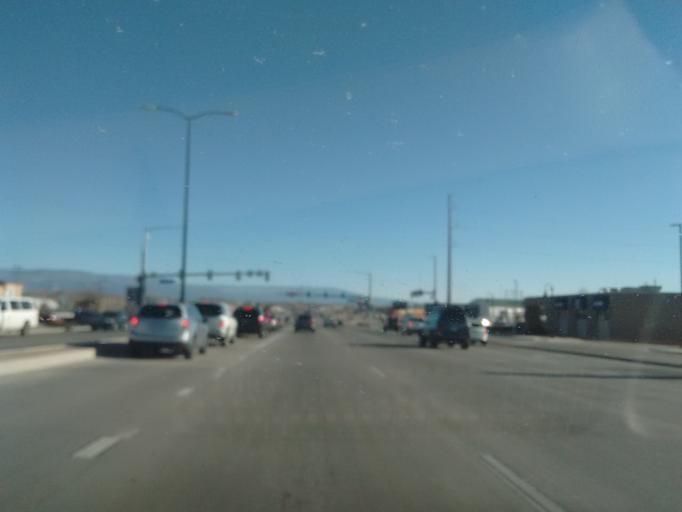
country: US
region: Colorado
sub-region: Mesa County
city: Grand Junction
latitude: 39.0834
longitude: -108.5903
